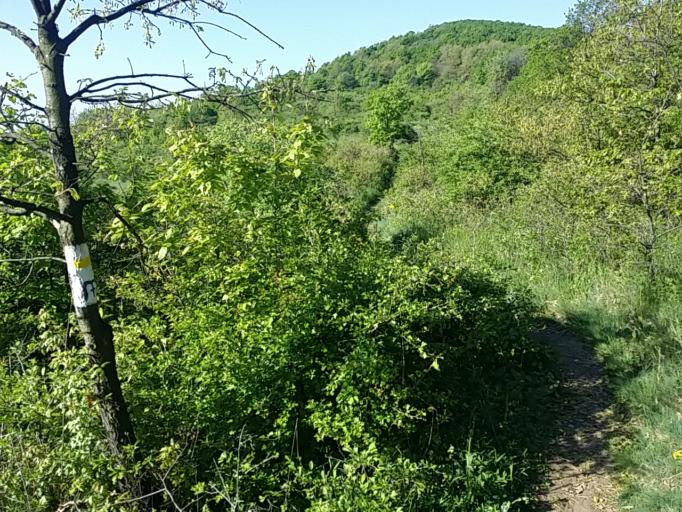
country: HU
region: Heves
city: Abasar
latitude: 47.8012
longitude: 19.9856
